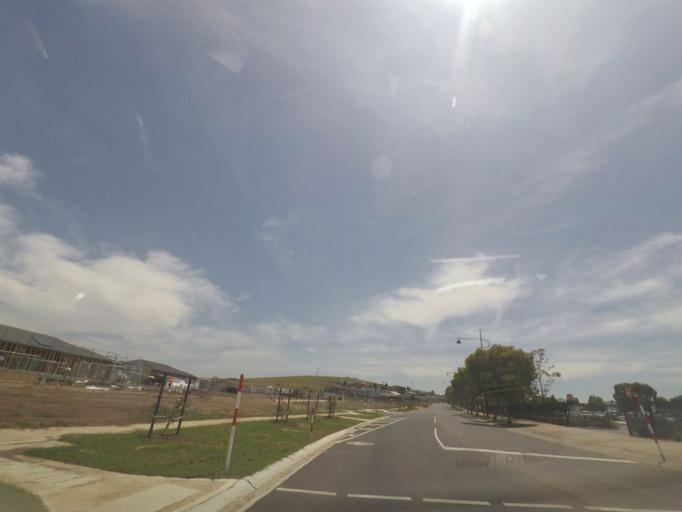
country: AU
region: Victoria
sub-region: Hume
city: Roxburgh Park
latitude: -37.6155
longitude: 144.9089
